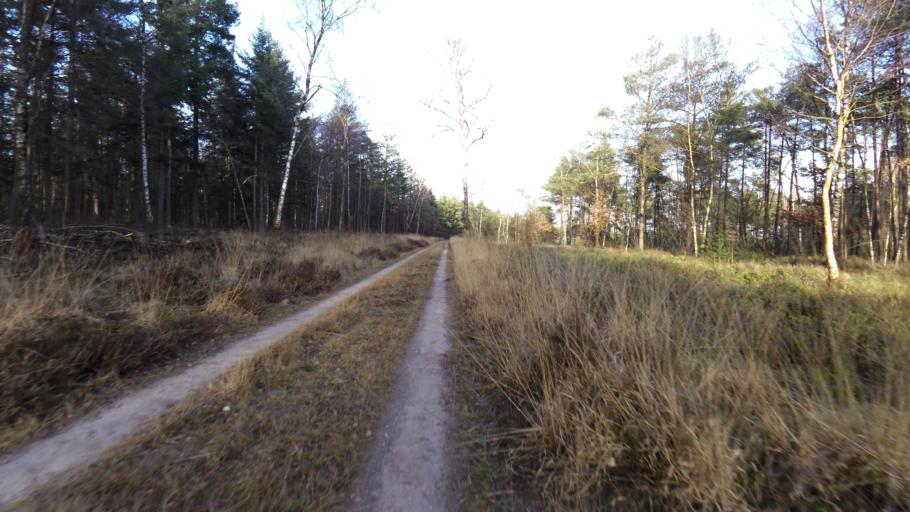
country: NL
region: Gelderland
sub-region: Gemeente Epe
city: Vaassen
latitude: 52.2732
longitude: 5.9094
